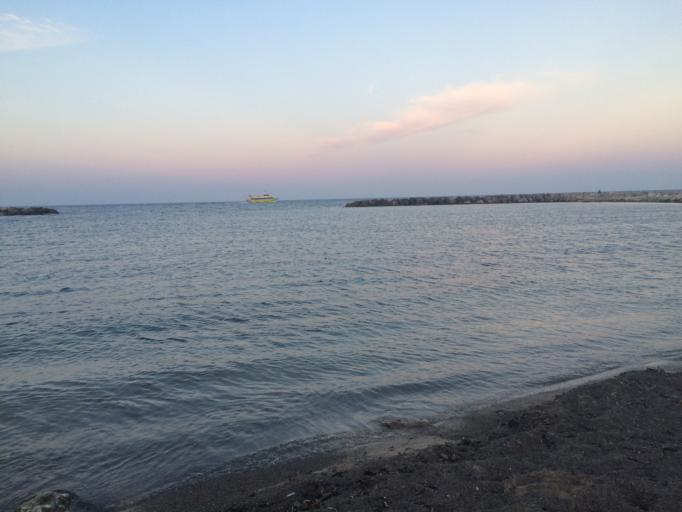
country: ES
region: Balearic Islands
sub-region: Illes Balears
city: Son Servera
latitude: 39.6114
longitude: 3.3912
